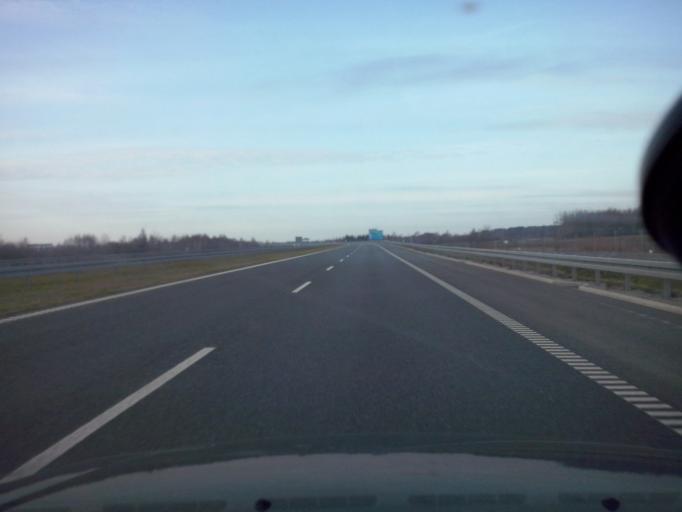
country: PL
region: Subcarpathian Voivodeship
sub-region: Powiat rzeszowski
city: Rudna Mala
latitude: 50.1054
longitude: 21.9971
